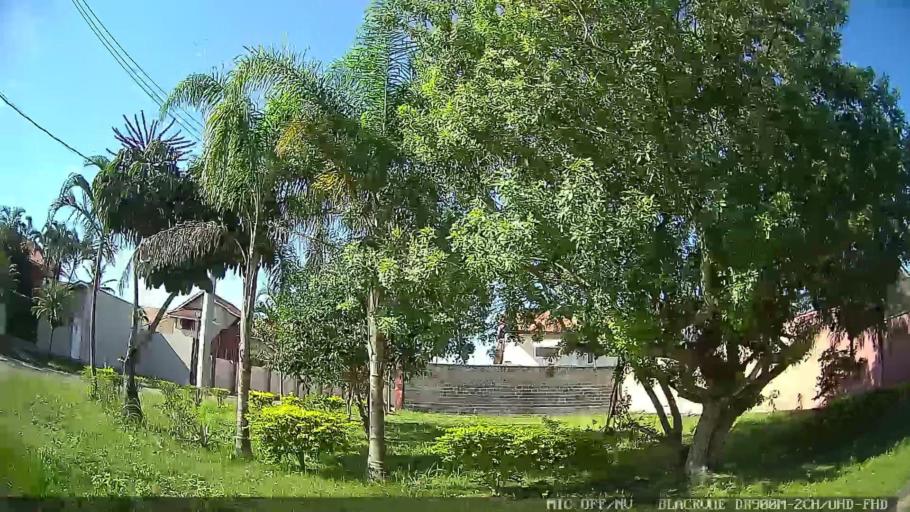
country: BR
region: Sao Paulo
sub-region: Peruibe
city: Peruibe
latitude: -24.2831
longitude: -46.9579
